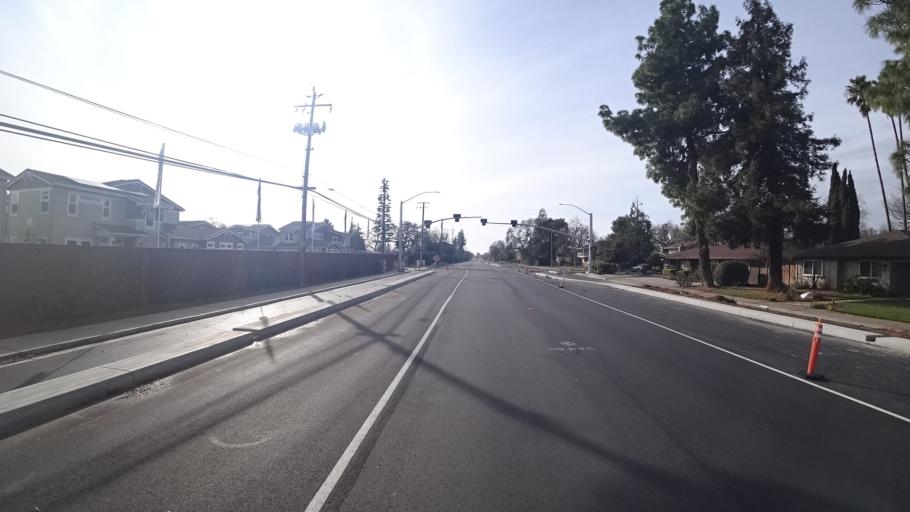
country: US
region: California
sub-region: Yolo County
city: Davis
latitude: 38.5445
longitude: -121.6945
